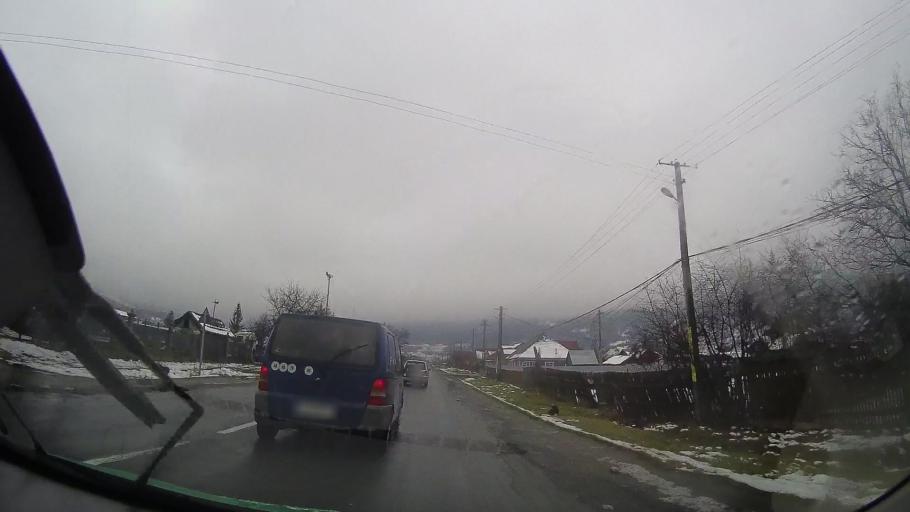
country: RO
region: Neamt
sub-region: Comuna Pangarati
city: Stejaru
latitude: 46.9125
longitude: 26.1820
